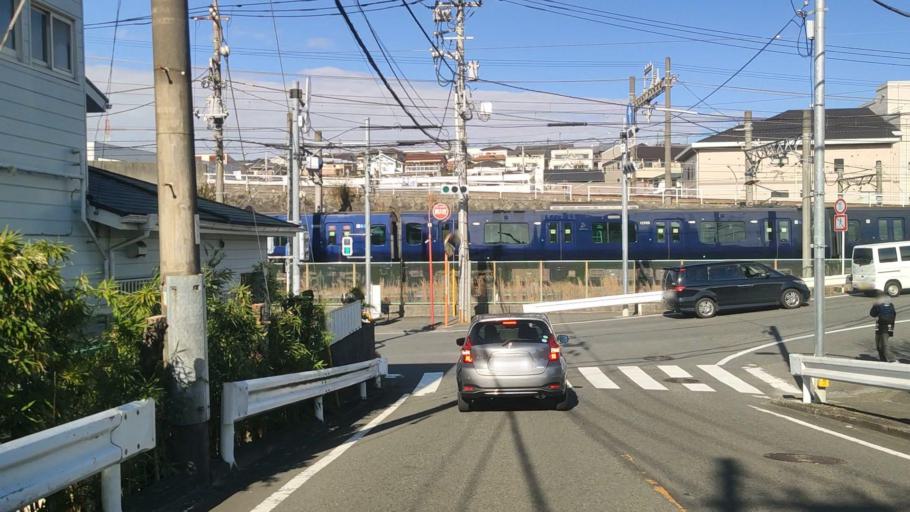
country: JP
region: Kanagawa
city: Minami-rinkan
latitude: 35.4606
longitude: 139.5288
